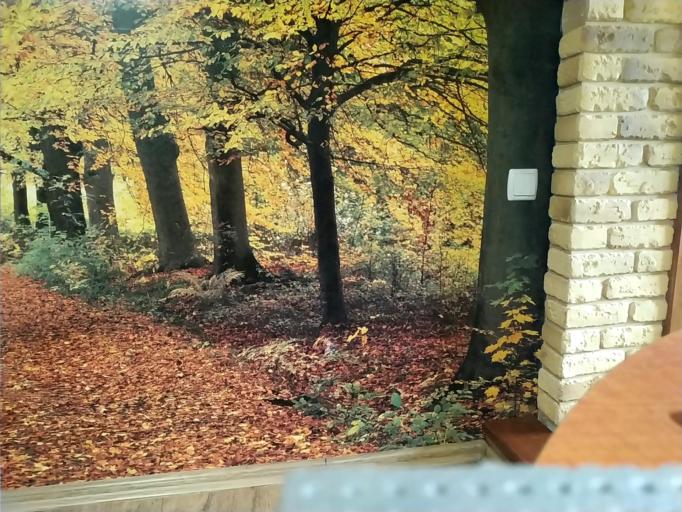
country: RU
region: Tverskaya
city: Kalashnikovo
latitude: 57.2718
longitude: 35.2371
